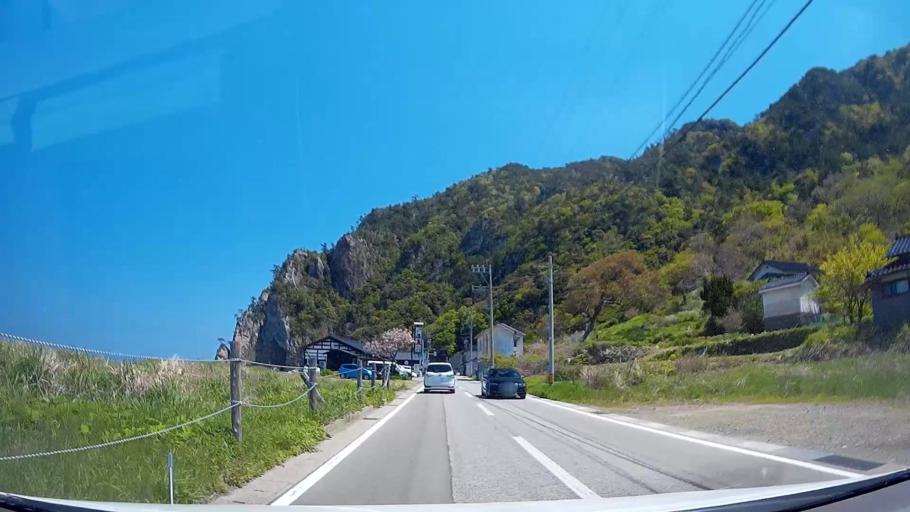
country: JP
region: Ishikawa
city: Nanao
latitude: 37.4604
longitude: 137.0790
